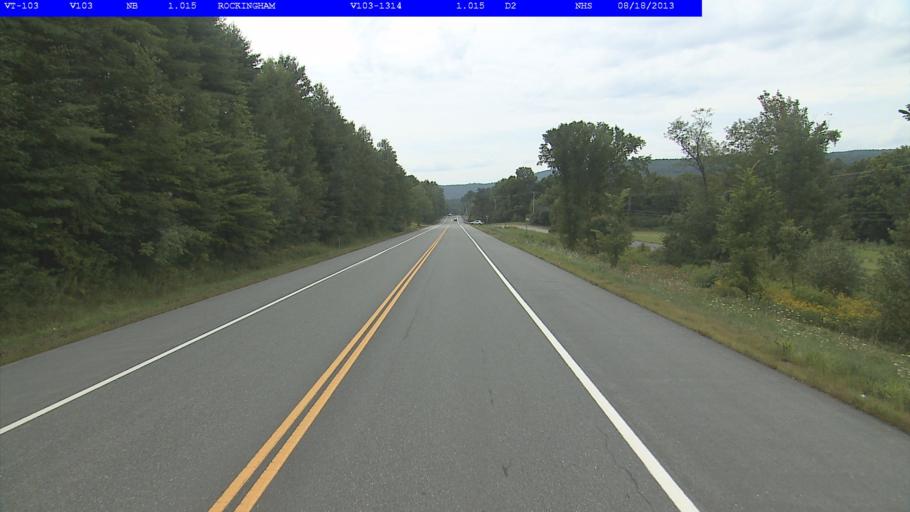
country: US
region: Vermont
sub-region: Windham County
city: Rockingham
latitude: 43.1841
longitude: -72.4771
